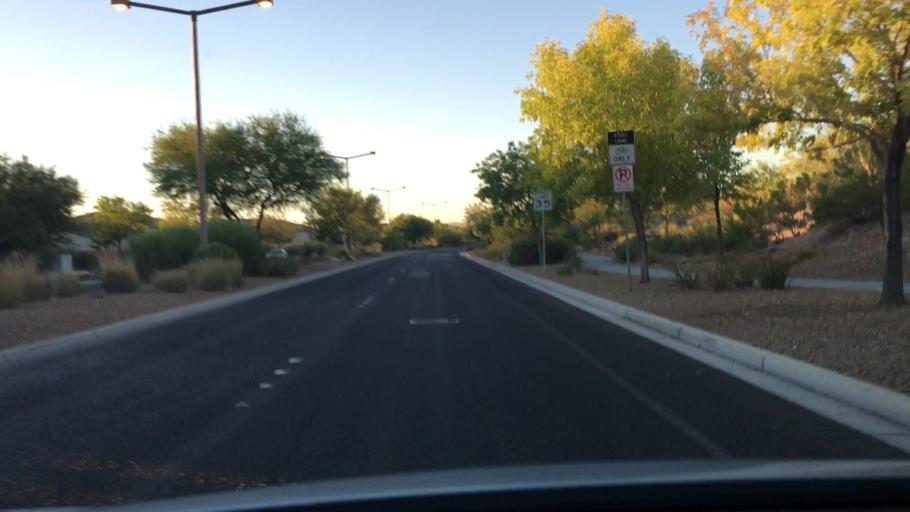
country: US
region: Nevada
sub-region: Clark County
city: Summerlin South
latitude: 36.1229
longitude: -115.3361
